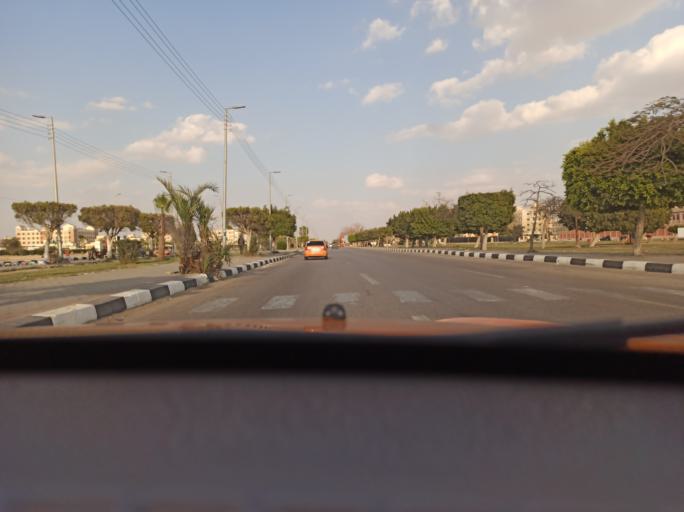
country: EG
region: Al Isma'iliyah
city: Ismailia
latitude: 30.6199
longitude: 32.2792
